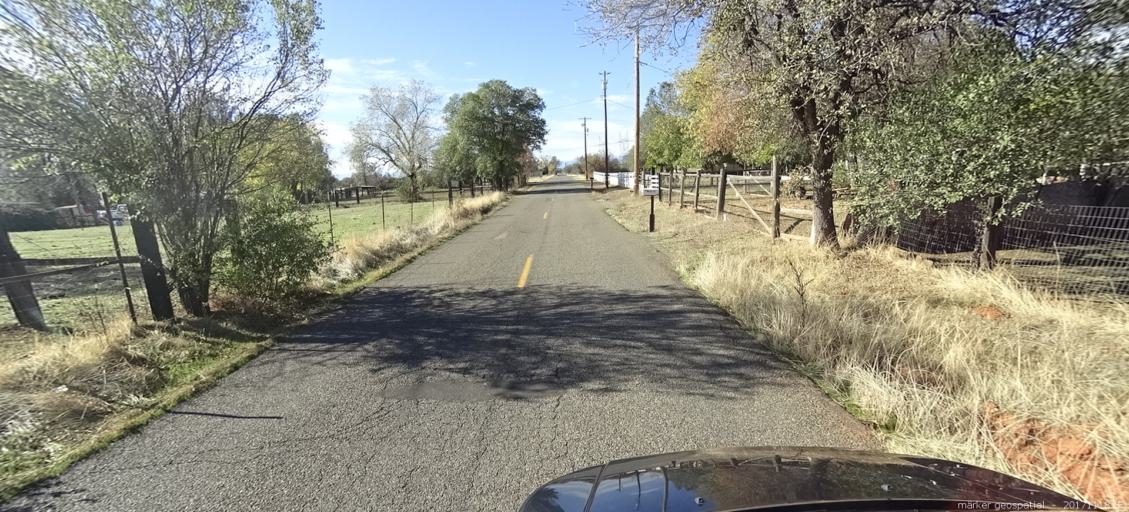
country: US
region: California
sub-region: Shasta County
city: Anderson
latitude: 40.4394
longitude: -122.4110
